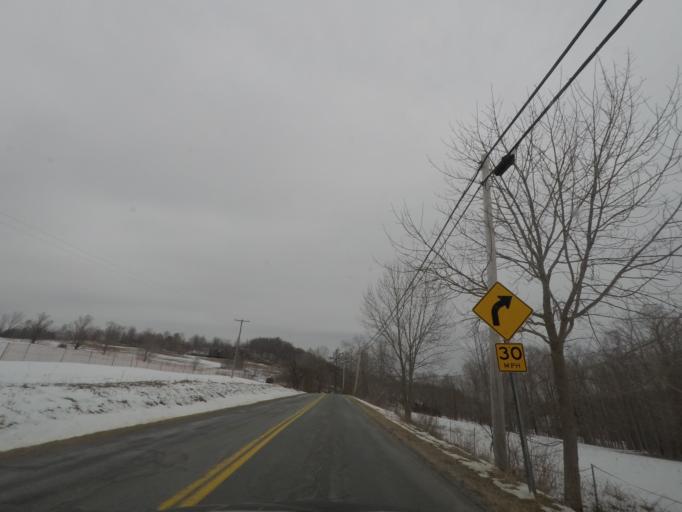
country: US
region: Massachusetts
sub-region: Berkshire County
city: Lanesborough
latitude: 42.5668
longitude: -73.3802
